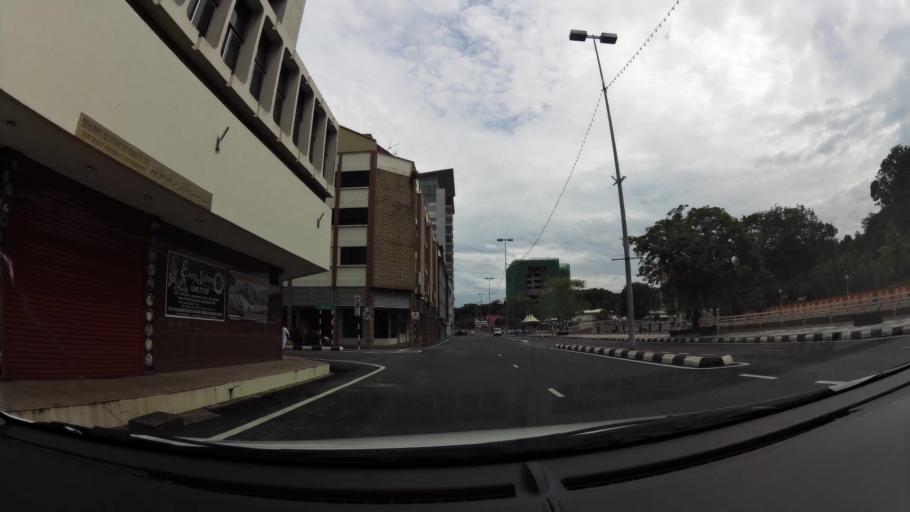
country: BN
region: Brunei and Muara
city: Bandar Seri Begawan
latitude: 4.8880
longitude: 114.9443
